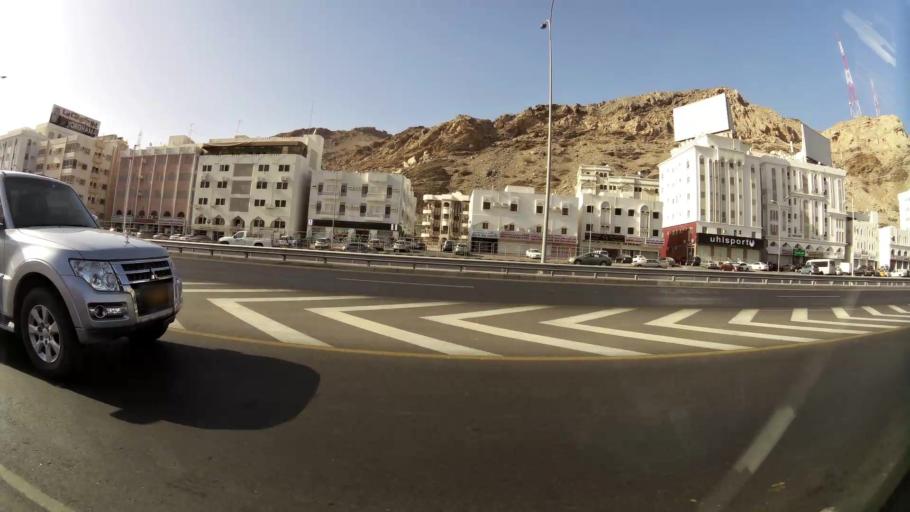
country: OM
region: Muhafazat Masqat
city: Muscat
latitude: 23.5907
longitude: 58.5301
